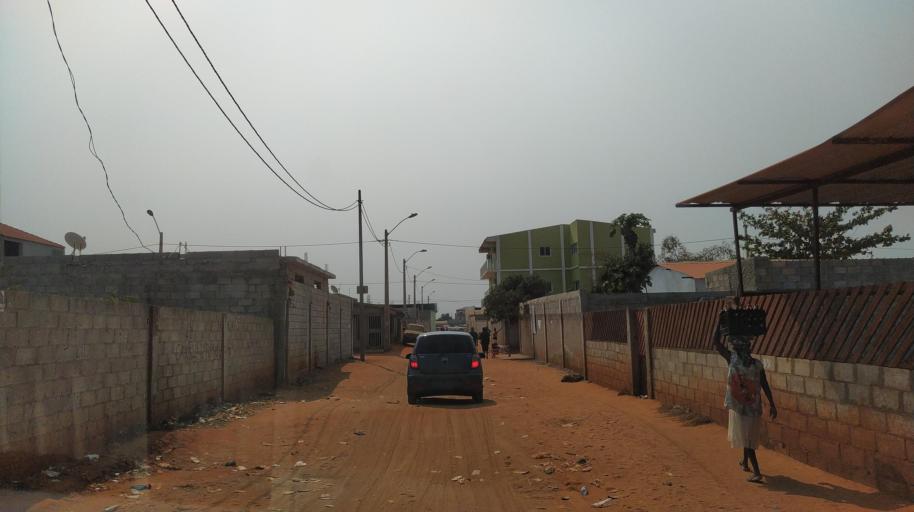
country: AO
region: Luanda
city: Luanda
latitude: -9.0640
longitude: 13.4173
